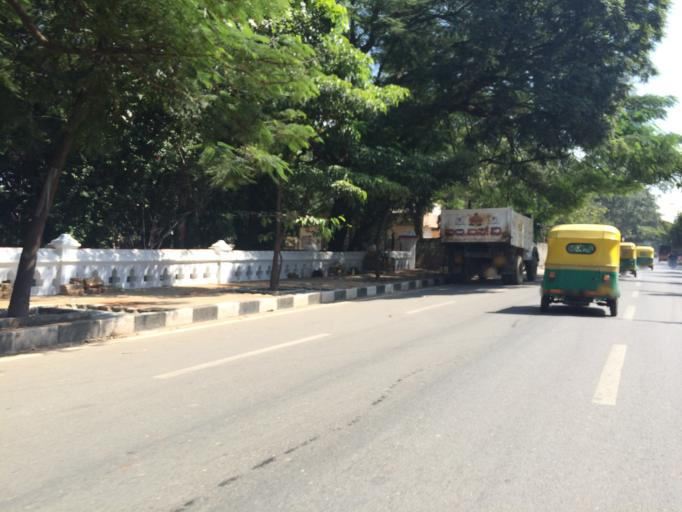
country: IN
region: Karnataka
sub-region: Bangalore Urban
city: Bangalore
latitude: 12.9788
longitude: 77.6039
